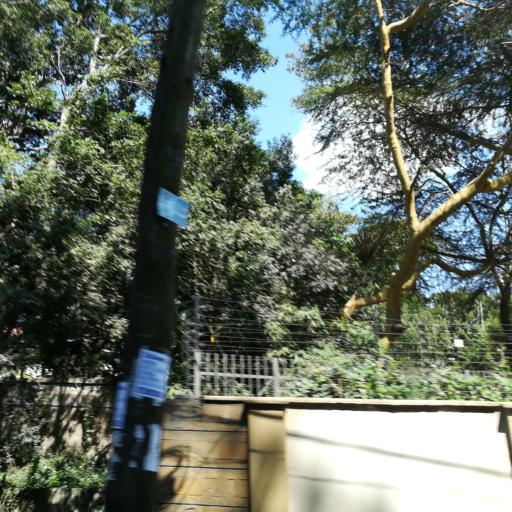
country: KE
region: Nairobi Area
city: Nairobi
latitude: -1.2954
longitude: 36.7952
